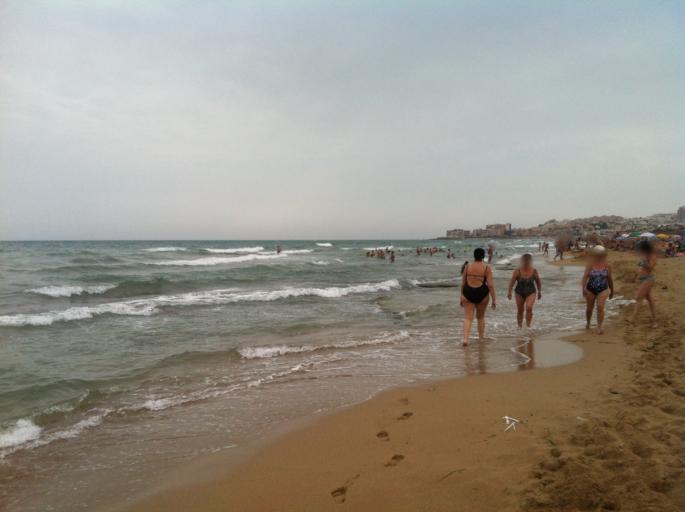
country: ES
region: Valencia
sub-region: Provincia de Alicante
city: Torrevieja
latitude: 38.0219
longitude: -0.6528
